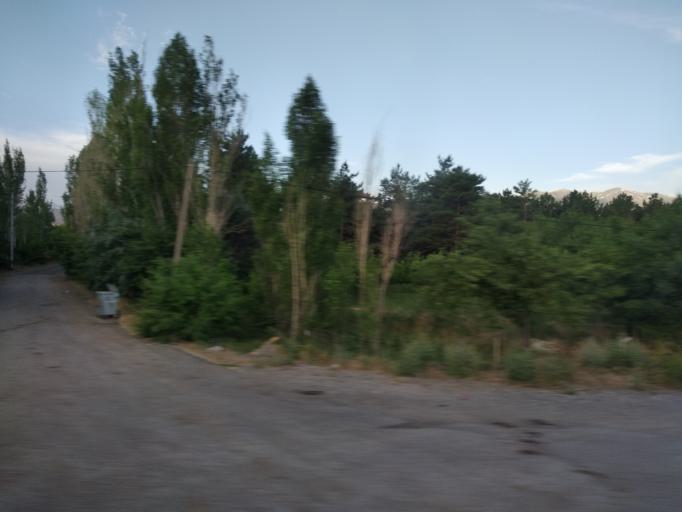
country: TR
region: Erzincan
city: Catalarmut
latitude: 39.8086
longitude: 39.3629
